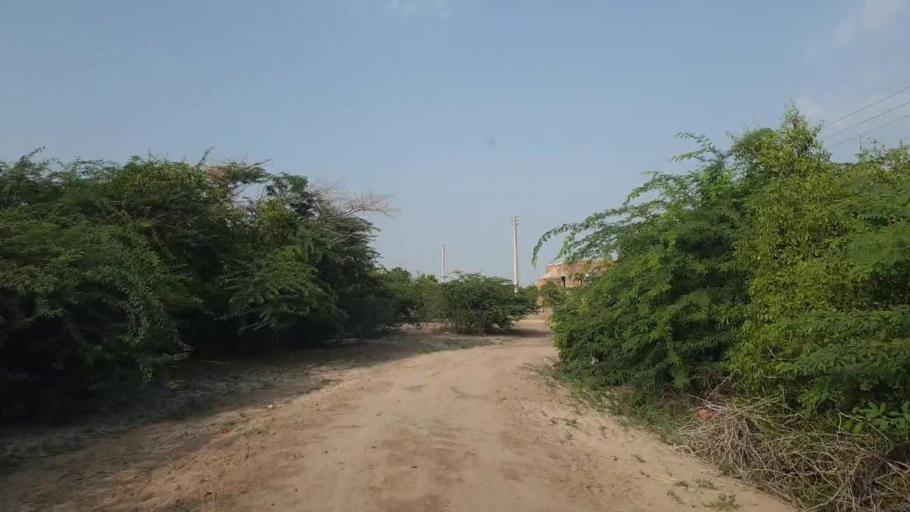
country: PK
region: Sindh
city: Kadhan
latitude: 24.4566
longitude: 68.8143
